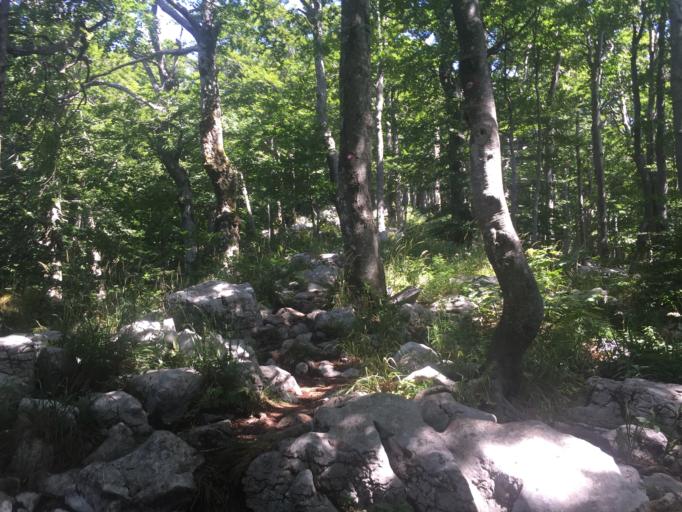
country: SI
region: Ajdovscina
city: Lokavec
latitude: 45.9778
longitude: 13.8603
